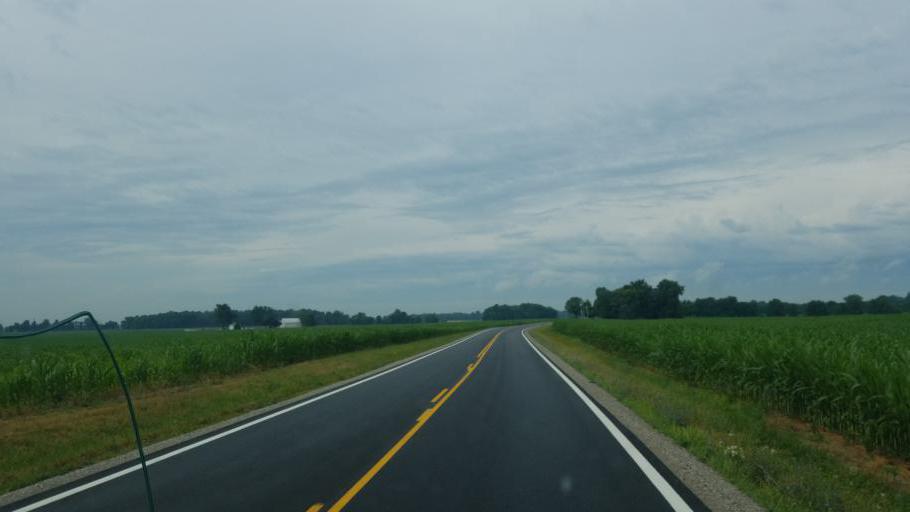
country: US
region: Ohio
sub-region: Defiance County
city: Hicksville
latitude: 41.3448
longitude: -84.6789
